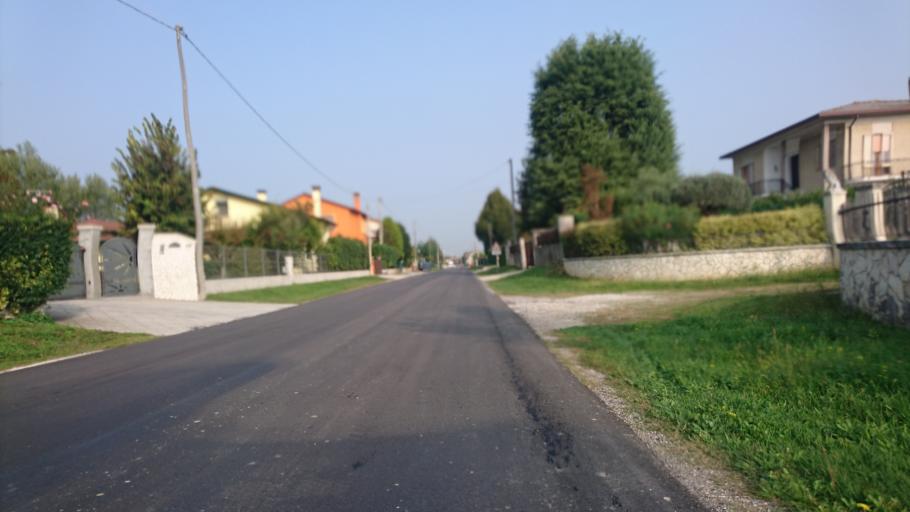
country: IT
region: Veneto
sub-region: Provincia di Padova
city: Curtarolo
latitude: 45.5309
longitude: 11.8408
